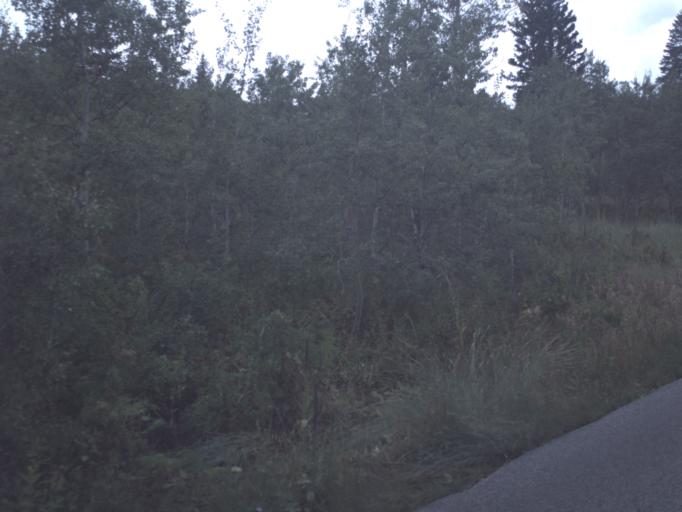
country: US
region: Utah
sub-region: Utah County
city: Lindon
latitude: 40.4099
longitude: -111.6052
